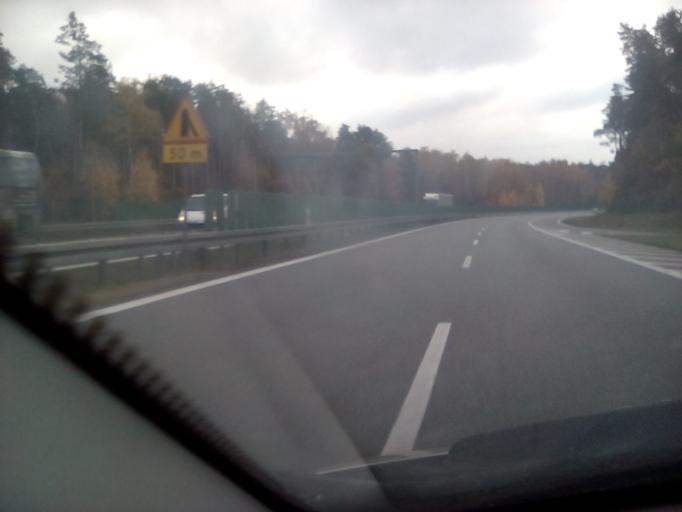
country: PL
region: Masovian Voivodeship
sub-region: Powiat bialobrzeski
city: Bialobrzegi
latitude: 51.6489
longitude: 20.9726
